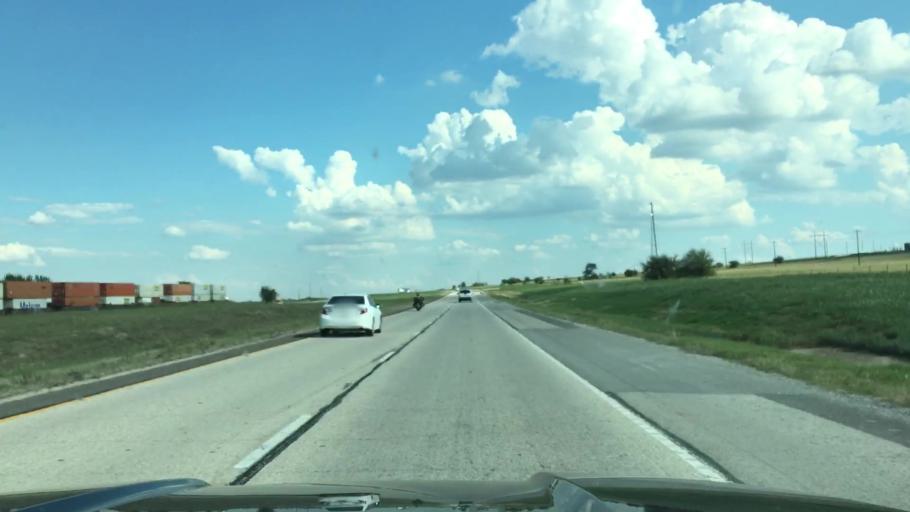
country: US
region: Texas
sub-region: Wise County
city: Boyd
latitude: 33.1595
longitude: -97.5238
